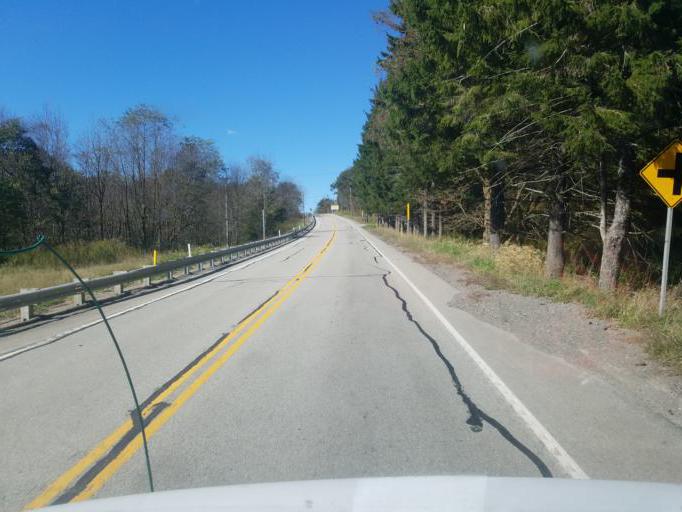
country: US
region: Pennsylvania
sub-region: Westmoreland County
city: Waterford
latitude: 40.1783
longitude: -79.1286
